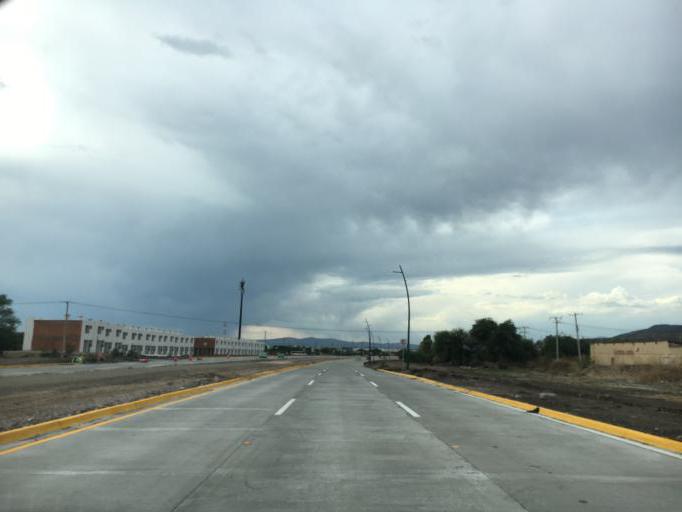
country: MX
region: Guanajuato
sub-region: Leon
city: Fraccionamiento Paraiso Real
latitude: 21.1121
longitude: -101.5869
